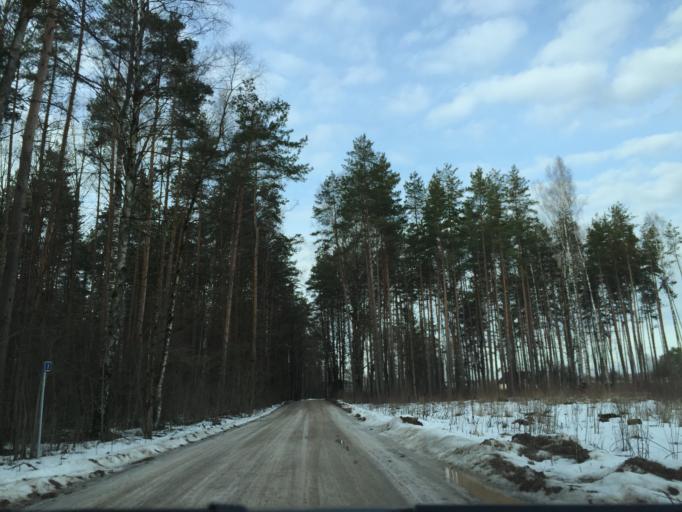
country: LV
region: Stopini
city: Ulbroka
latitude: 56.9245
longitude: 24.2842
